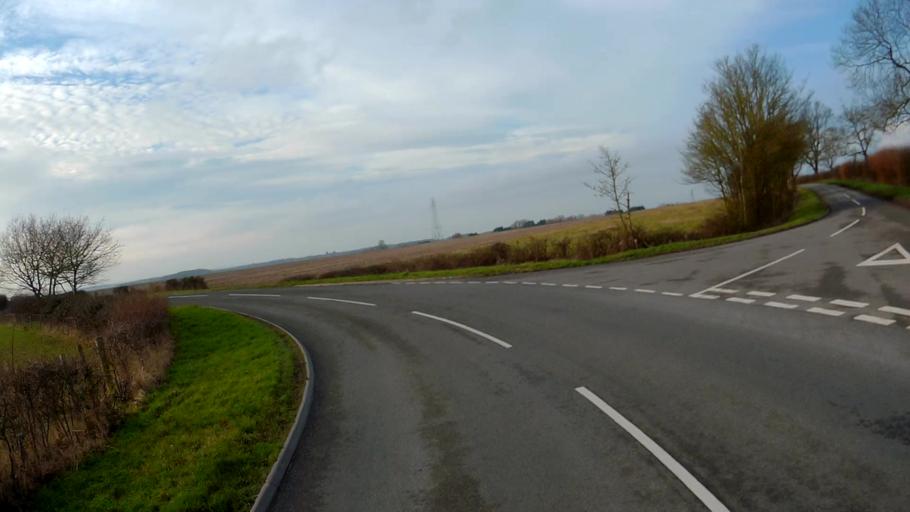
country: GB
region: England
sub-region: Lincolnshire
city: Bourne
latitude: 52.7380
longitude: -0.4000
